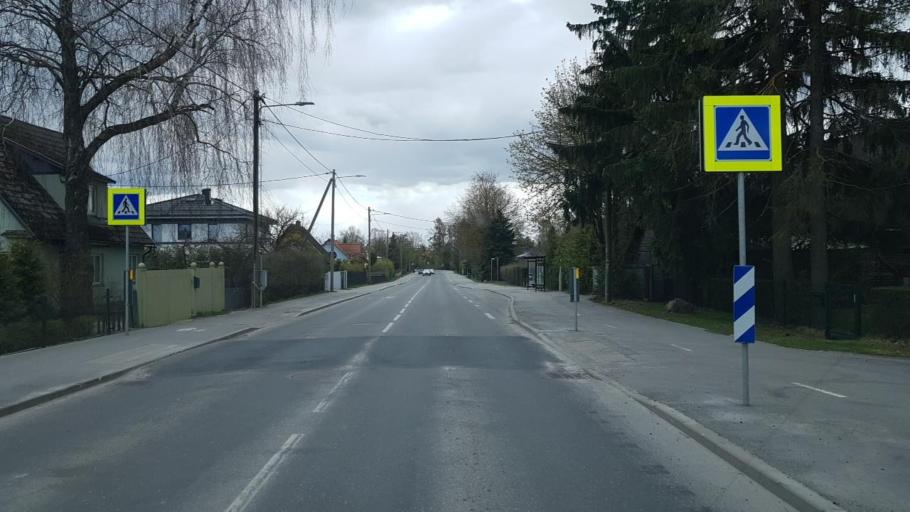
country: EE
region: Tartu
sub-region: Tartu linn
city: Tartu
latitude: 58.3598
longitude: 26.7026
